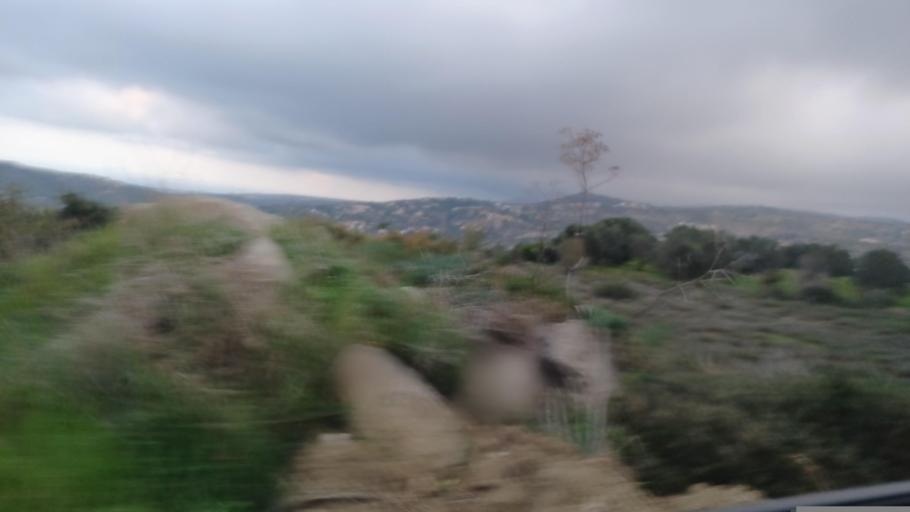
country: CY
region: Pafos
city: Mesogi
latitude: 34.7846
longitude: 32.4975
